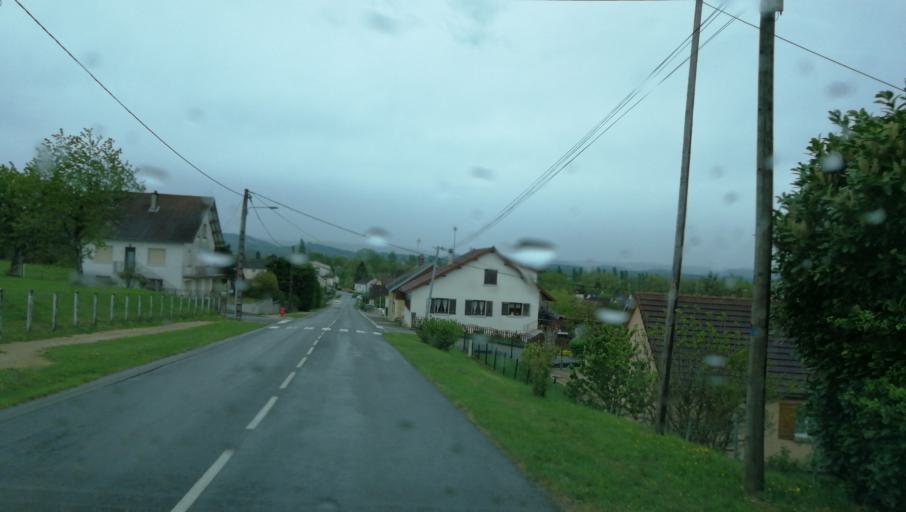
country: FR
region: Franche-Comte
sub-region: Departement du Jura
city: Bletterans
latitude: 46.7471
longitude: 5.4437
